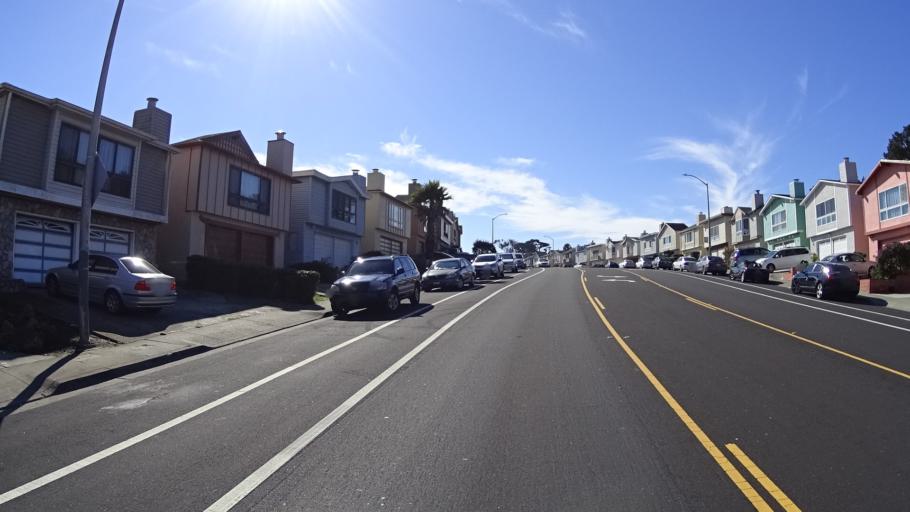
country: US
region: California
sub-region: San Mateo County
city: Colma
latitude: 37.6534
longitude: -122.4690
